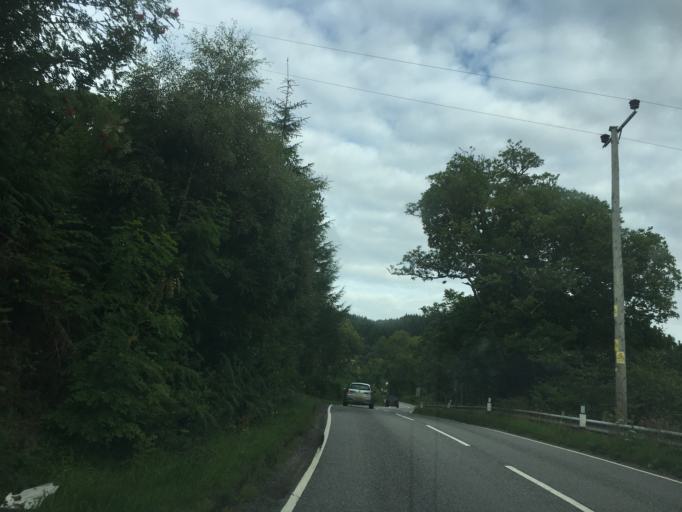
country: GB
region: Scotland
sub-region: Argyll and Bute
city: Oban
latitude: 56.3303
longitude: -5.5083
